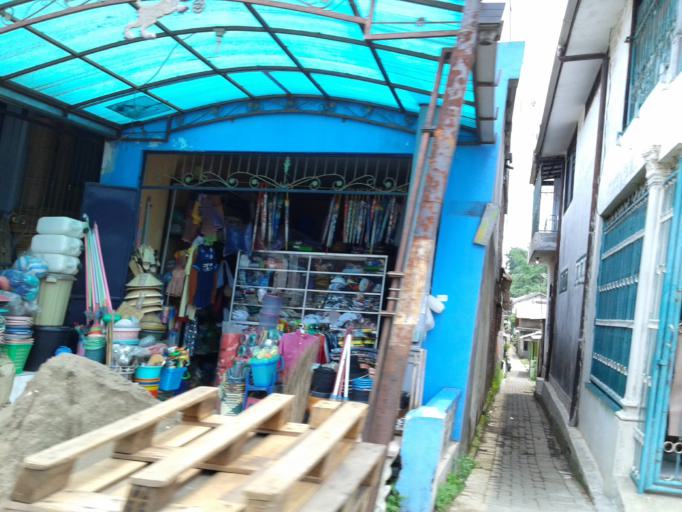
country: ID
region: East Java
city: Singosari
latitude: -7.9000
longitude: 112.6881
